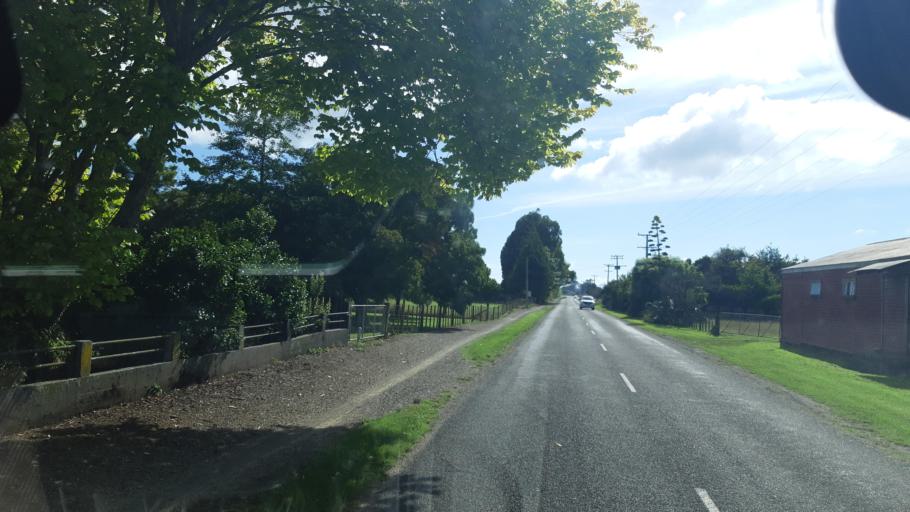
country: NZ
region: Tasman
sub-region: Tasman District
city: Richmond
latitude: -41.3066
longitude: 173.1509
